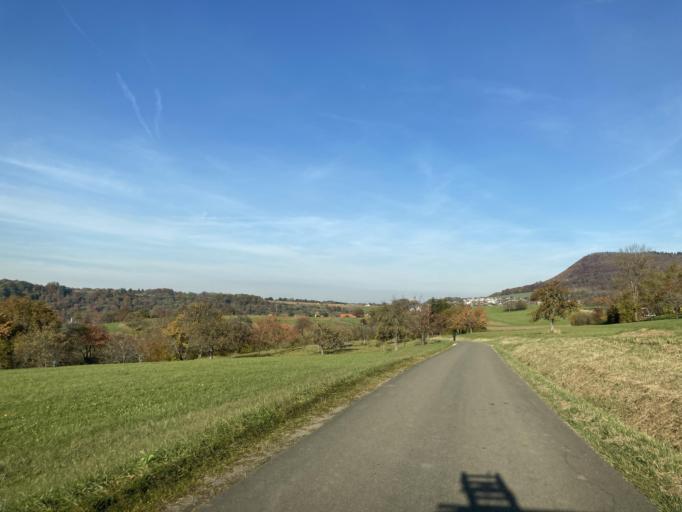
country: DE
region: Baden-Wuerttemberg
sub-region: Tuebingen Region
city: Nehren
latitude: 48.4058
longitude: 9.0984
